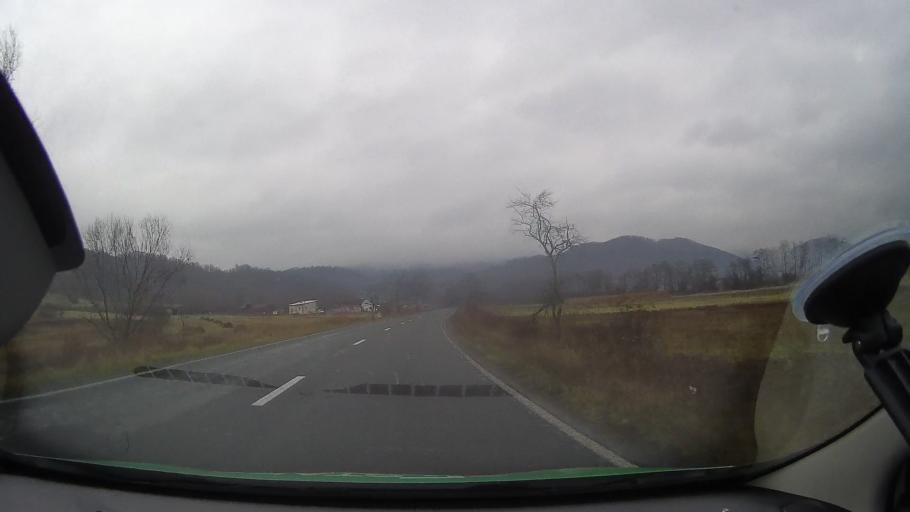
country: RO
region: Arad
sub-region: Comuna Plescuta
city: Plescuta
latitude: 46.2951
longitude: 22.4153
